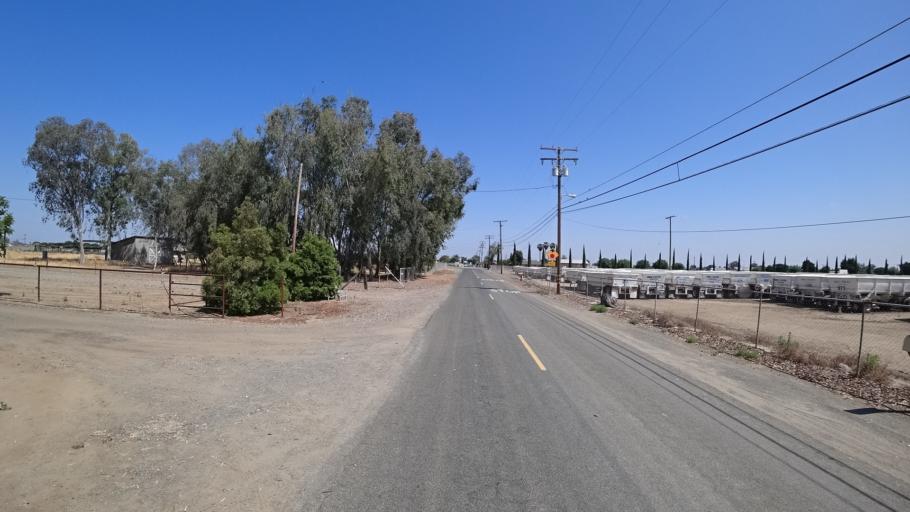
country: US
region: California
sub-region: Kings County
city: Home Garden
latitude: 36.3220
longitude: -119.6213
